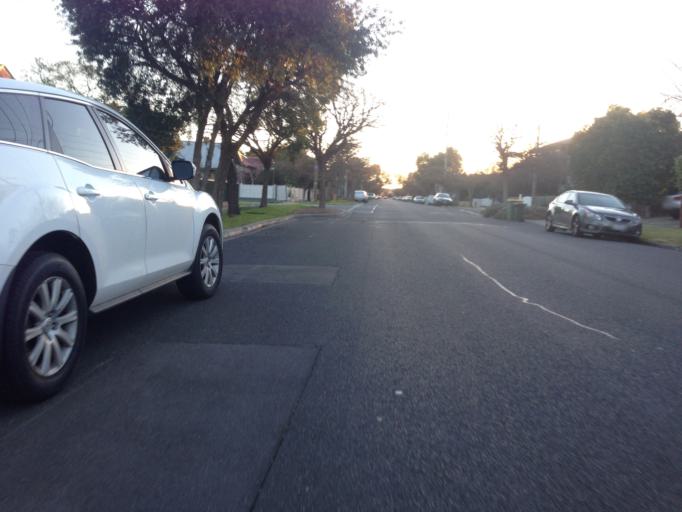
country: AU
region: Victoria
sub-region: Darebin
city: Fairfield
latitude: -37.7741
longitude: 145.0162
